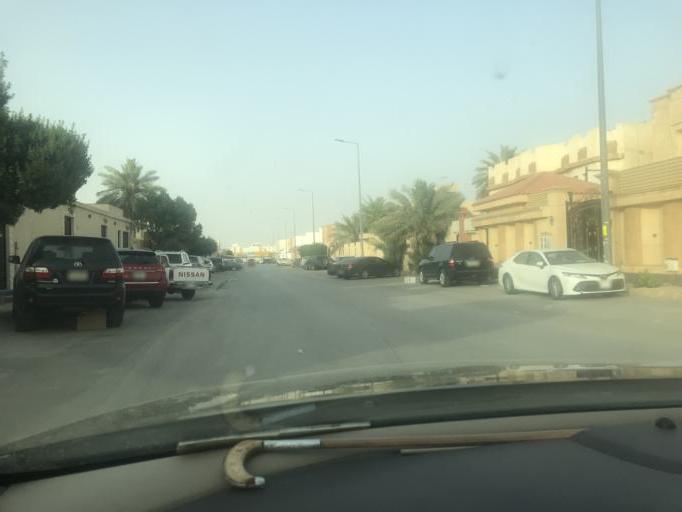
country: SA
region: Ar Riyad
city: Riyadh
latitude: 24.7421
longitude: 46.7746
